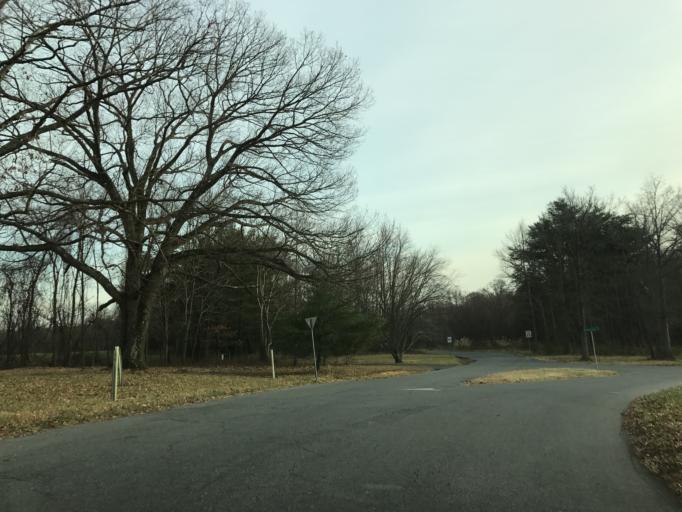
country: US
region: Maryland
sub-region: Baltimore County
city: White Marsh
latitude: 39.3885
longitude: -76.3979
